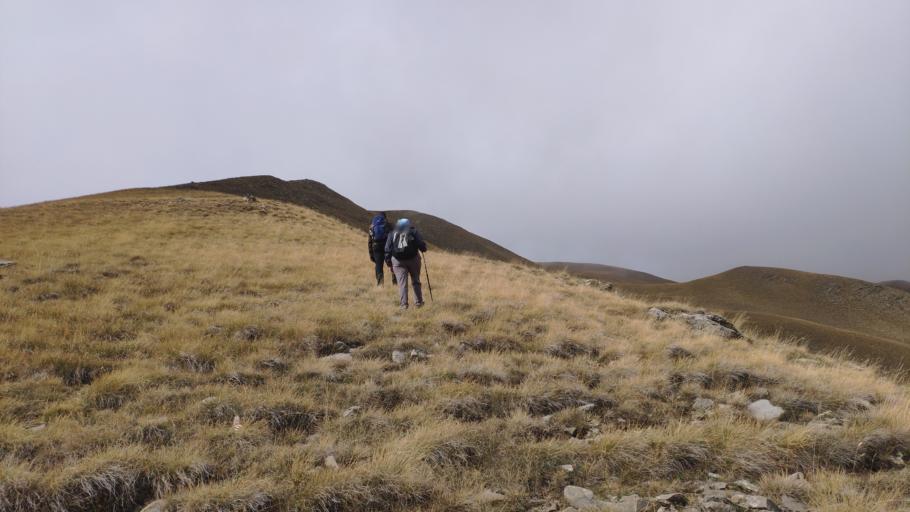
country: AL
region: Korce
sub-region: Rrethi i Kolonjes
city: Erseke
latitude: 40.3626
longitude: 20.7987
